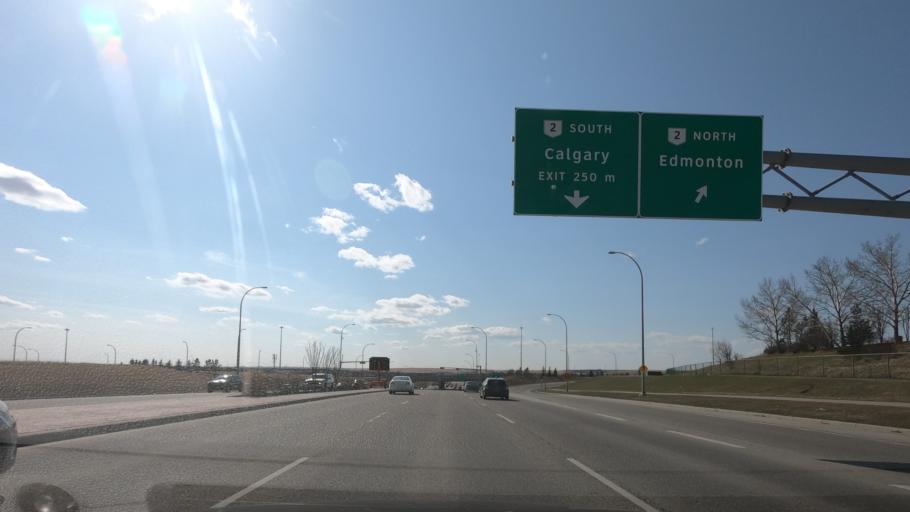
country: CA
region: Alberta
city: Airdrie
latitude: 51.2708
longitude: -113.9972
